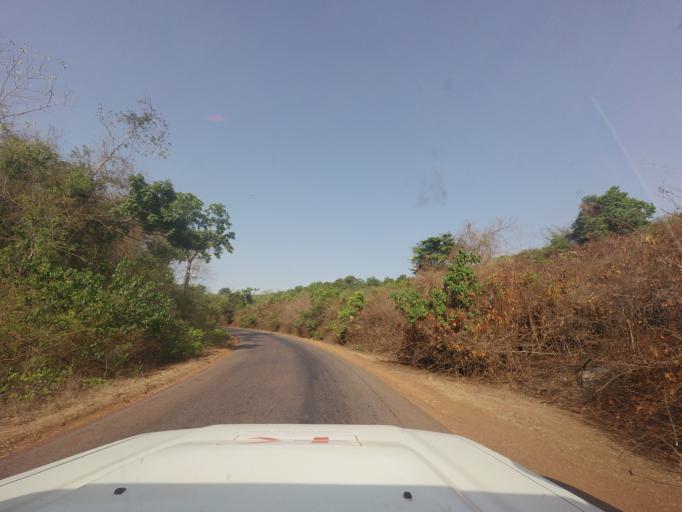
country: GN
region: Mamou
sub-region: Mamou Prefecture
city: Mamou
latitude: 10.3568
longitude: -12.1983
